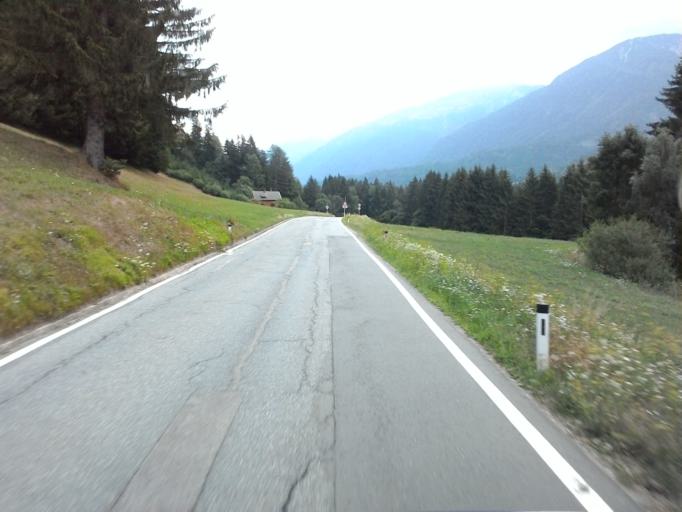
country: AT
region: Carinthia
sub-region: Politischer Bezirk Spittal an der Drau
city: Oberdrauburg
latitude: 46.6738
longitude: 12.9674
